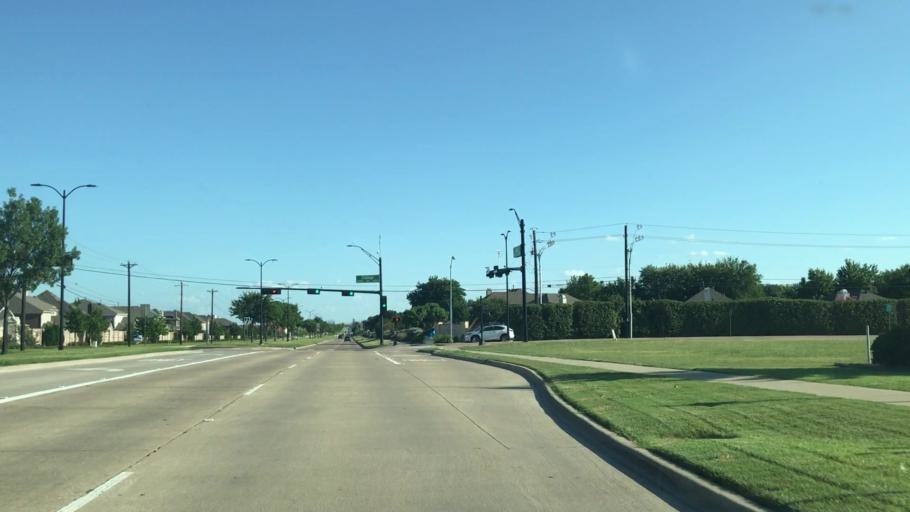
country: US
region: Texas
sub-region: Collin County
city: Frisco
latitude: 33.1311
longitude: -96.7681
